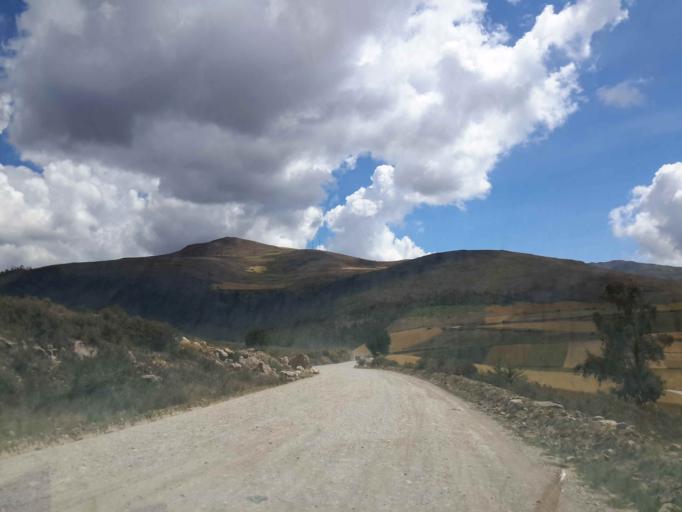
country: PE
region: Apurimac
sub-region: Provincia de Andahuaylas
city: Pacucha
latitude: -13.6346
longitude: -73.3419
